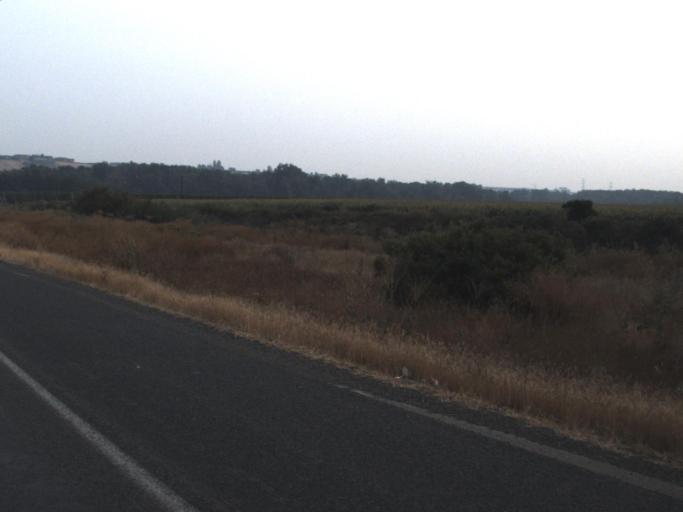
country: US
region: Washington
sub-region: Yakima County
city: Granger
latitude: 46.3298
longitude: -120.2031
